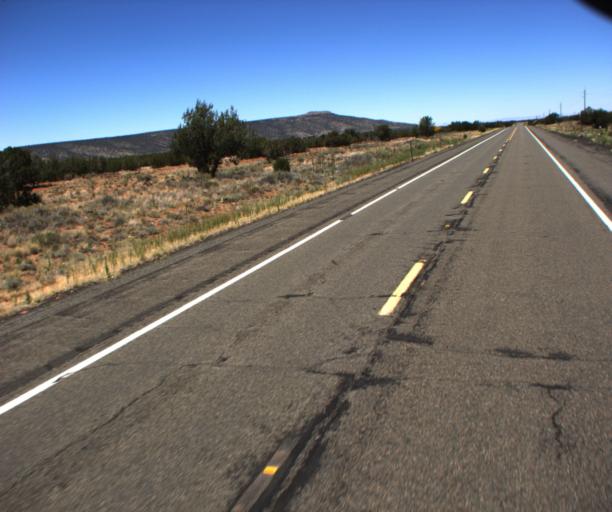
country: US
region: Arizona
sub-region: Coconino County
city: LeChee
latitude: 34.8164
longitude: -110.9659
